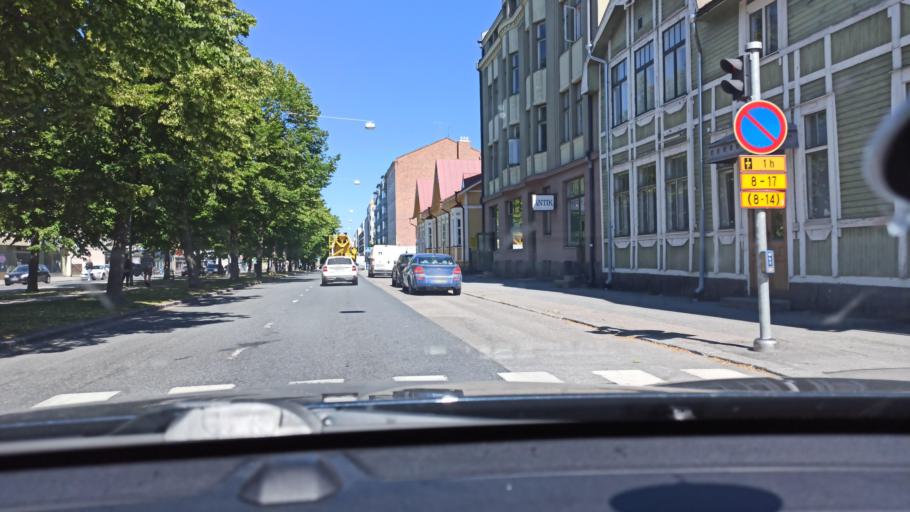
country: FI
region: Ostrobothnia
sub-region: Vaasa
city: Vaasa
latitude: 63.0908
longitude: 21.6205
